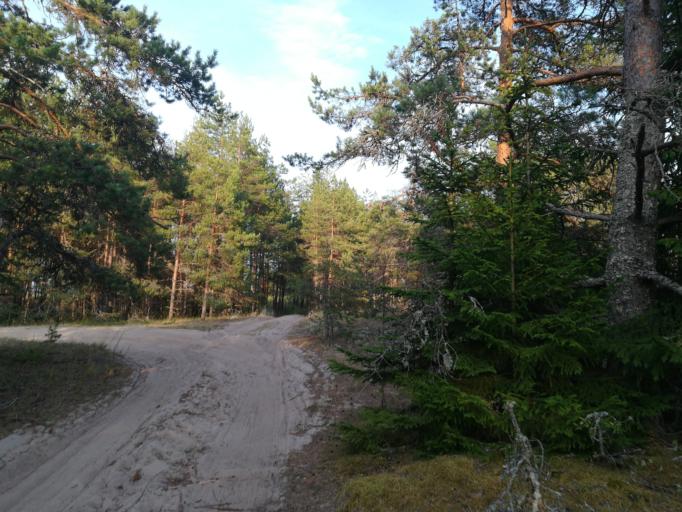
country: RU
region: Leningrad
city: Ust'-Luga
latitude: 59.6772
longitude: 28.2453
